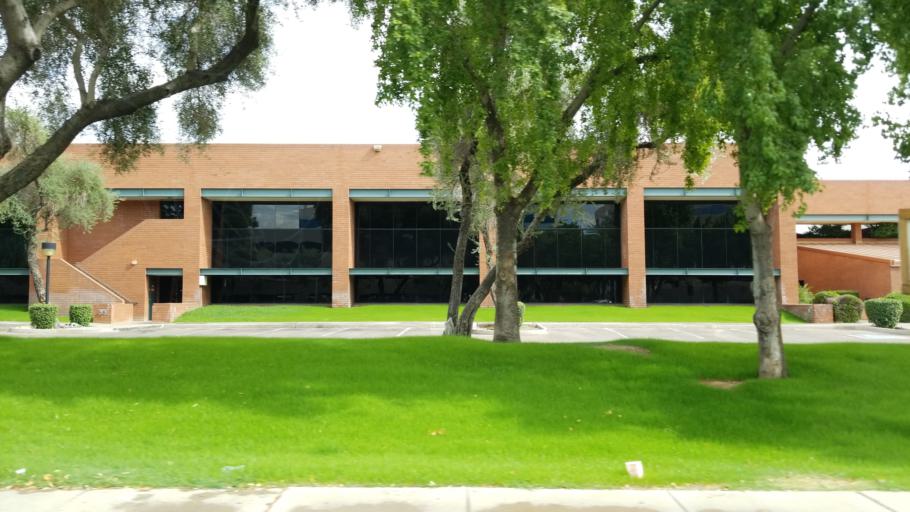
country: US
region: Arizona
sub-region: Maricopa County
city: Glendale
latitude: 33.5699
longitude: -112.1123
